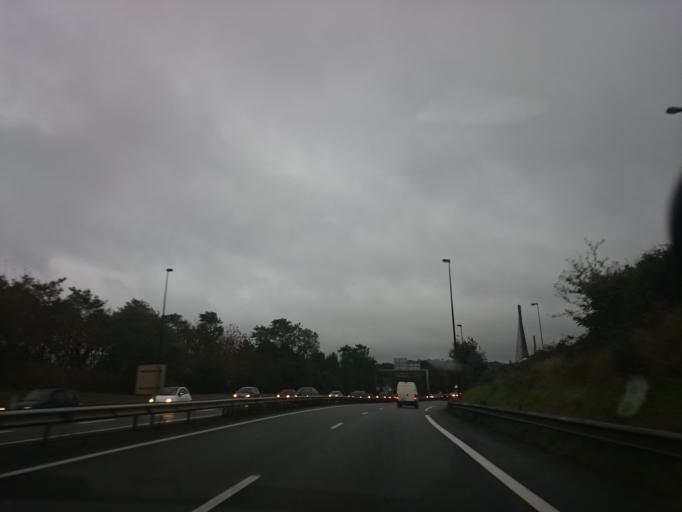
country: FR
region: Brittany
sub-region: Departement du Finistere
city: Le Relecq-Kerhuon
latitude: 48.3941
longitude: -4.4059
